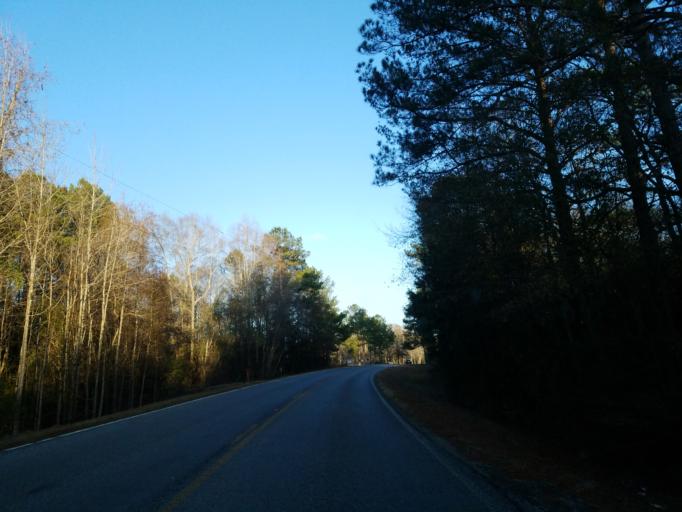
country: US
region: Mississippi
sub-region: Clarke County
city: Stonewall
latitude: 32.1661
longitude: -88.8583
